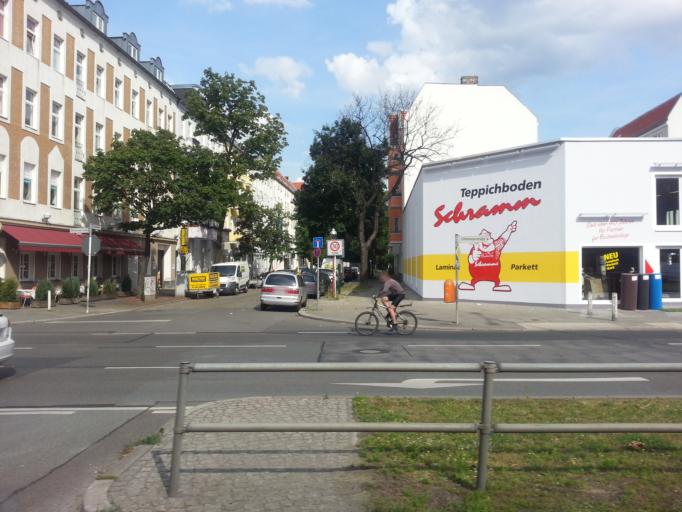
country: DE
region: Berlin
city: Reinickendorf
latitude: 52.5680
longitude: 13.3294
